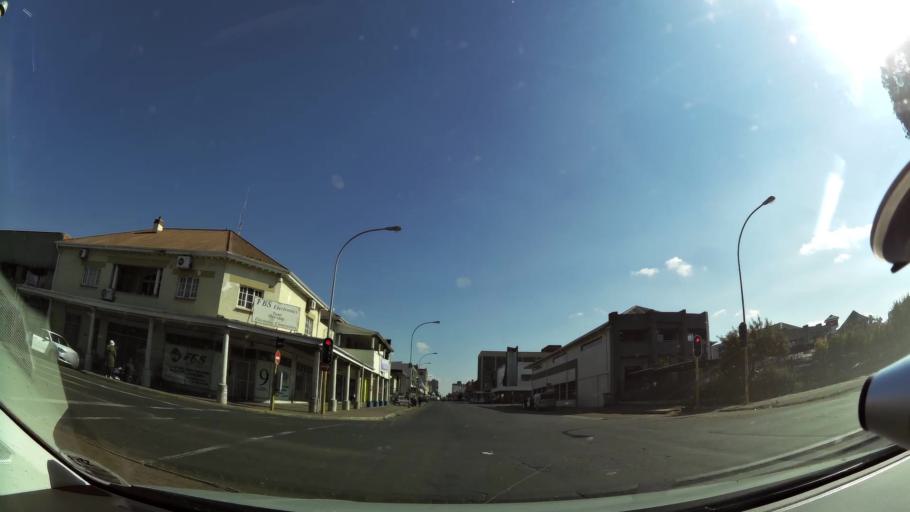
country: ZA
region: Orange Free State
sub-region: Mangaung Metropolitan Municipality
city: Bloemfontein
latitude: -29.1152
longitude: 26.2259
